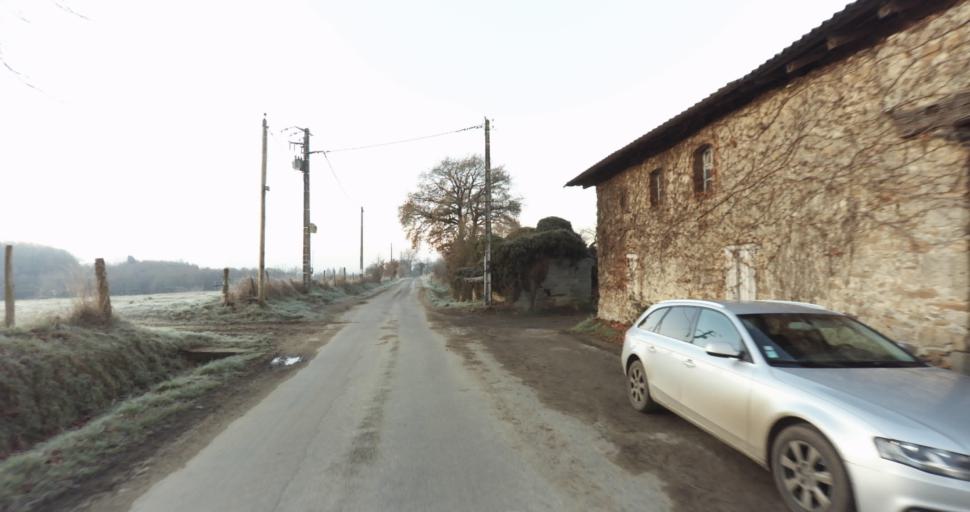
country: FR
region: Limousin
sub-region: Departement de la Haute-Vienne
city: Aixe-sur-Vienne
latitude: 45.8076
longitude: 1.1303
